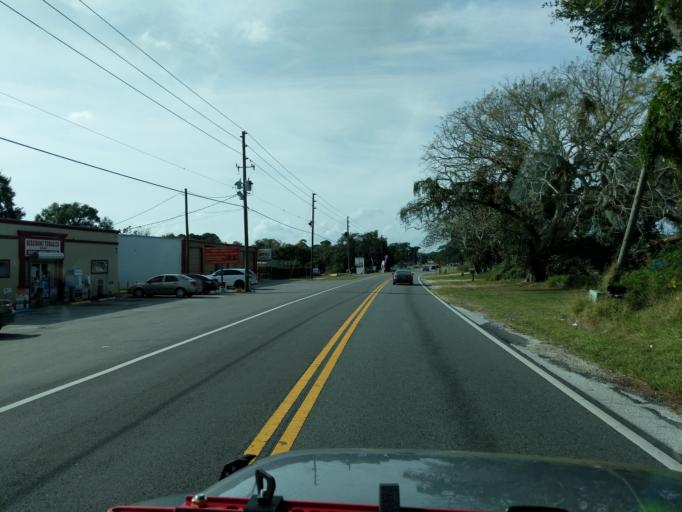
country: US
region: Florida
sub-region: Lake County
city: Tavares
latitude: 28.8031
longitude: -81.7032
